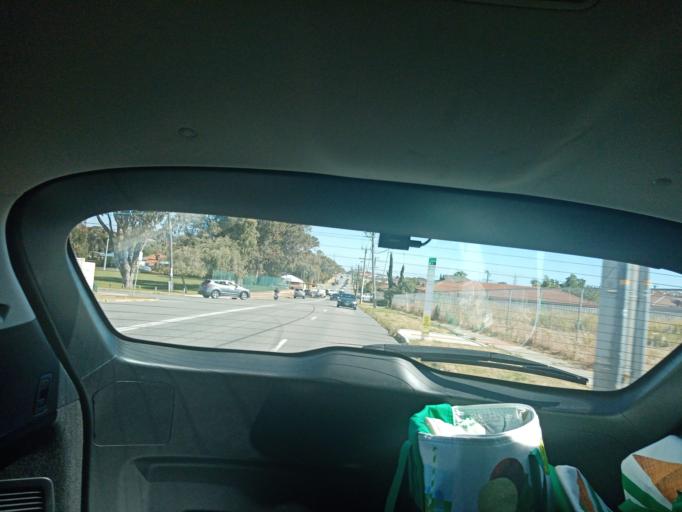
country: AU
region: Western Australia
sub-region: City of Cockburn
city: Spearwood
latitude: -32.1060
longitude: 115.7827
